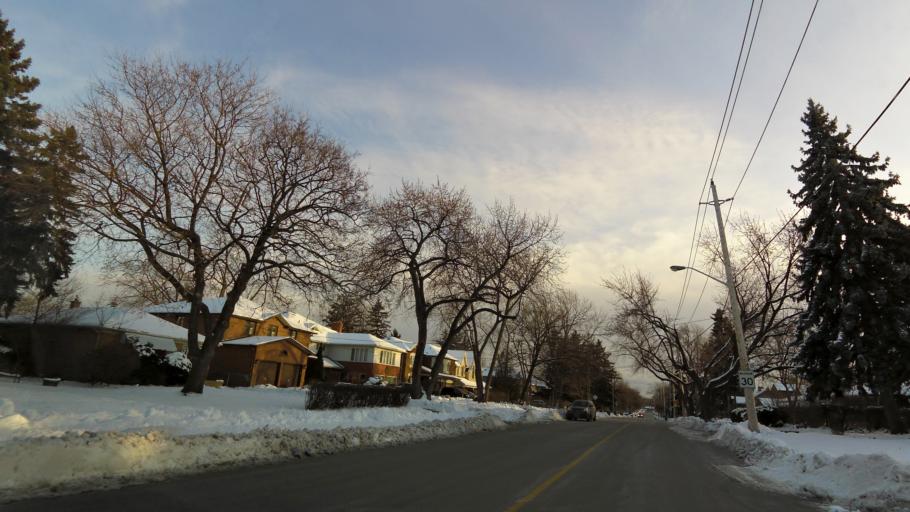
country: CA
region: Ontario
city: Etobicoke
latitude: 43.6445
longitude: -79.5501
